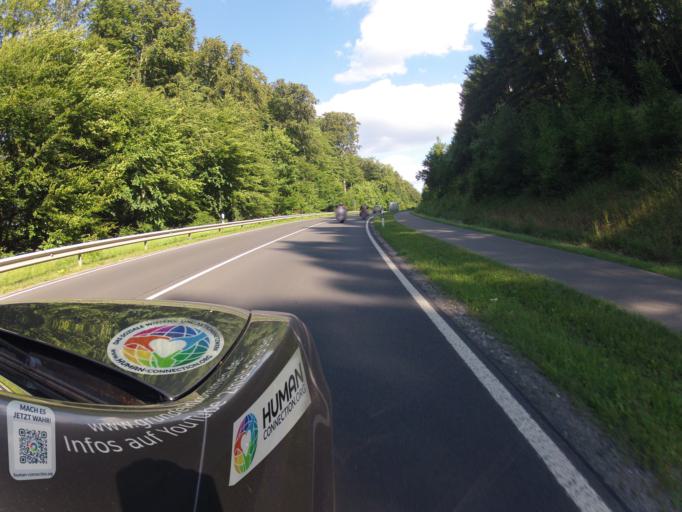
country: DE
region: Mecklenburg-Vorpommern
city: Seebad Bansin
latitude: 53.9758
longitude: 14.1096
